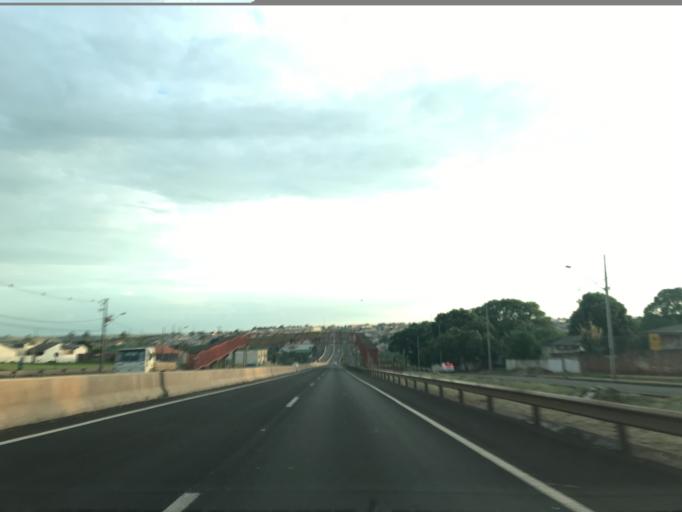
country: BR
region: Parana
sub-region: Maringa
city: Maringa
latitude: -23.3919
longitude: -51.9708
